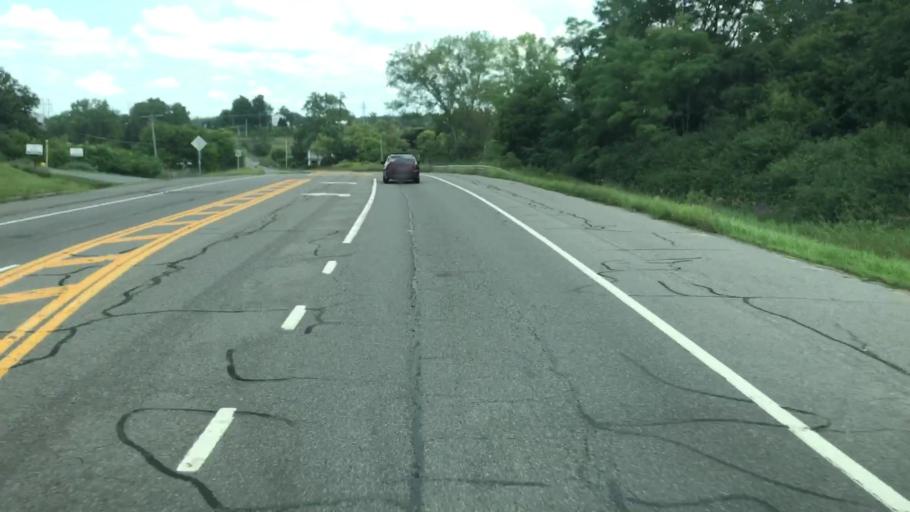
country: US
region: New York
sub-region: Onondaga County
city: Westvale
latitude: 42.9944
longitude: -76.2154
